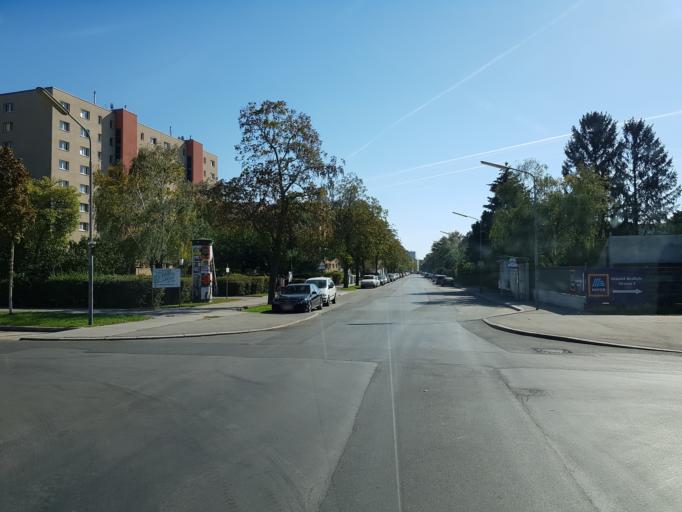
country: AT
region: Lower Austria
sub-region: Politischer Bezirk Wien-Umgebung
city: Gerasdorf bei Wien
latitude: 48.2736
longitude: 16.4421
